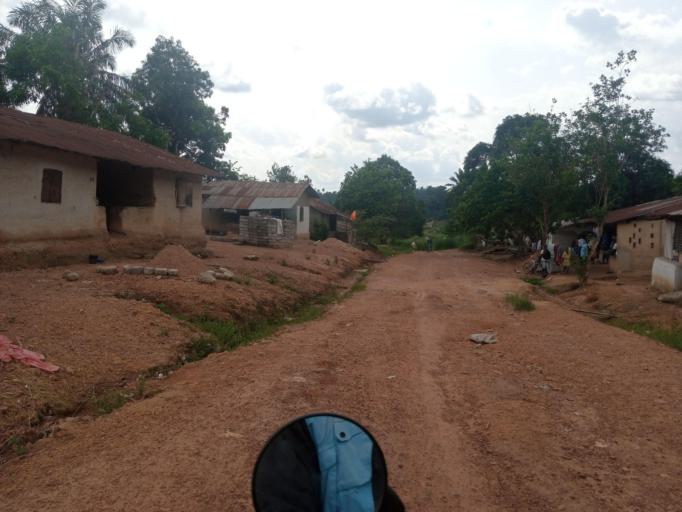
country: SL
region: Southern Province
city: Bo
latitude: 7.9897
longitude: -11.7439
